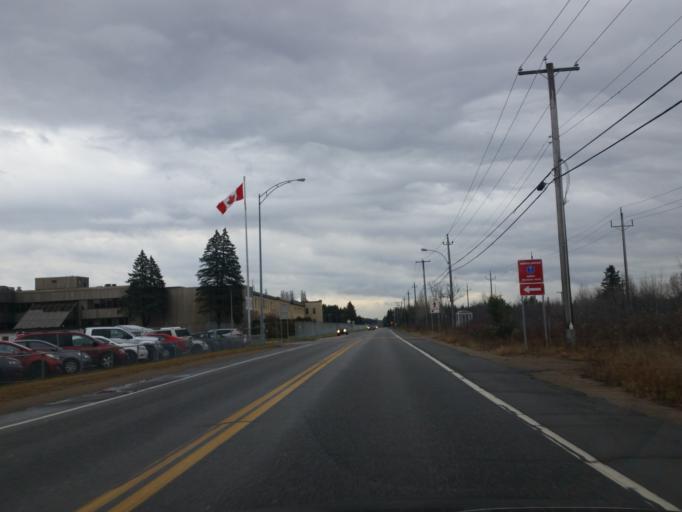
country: CA
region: Quebec
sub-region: Capitale-Nationale
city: Shannon
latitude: 46.8830
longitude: -71.4810
